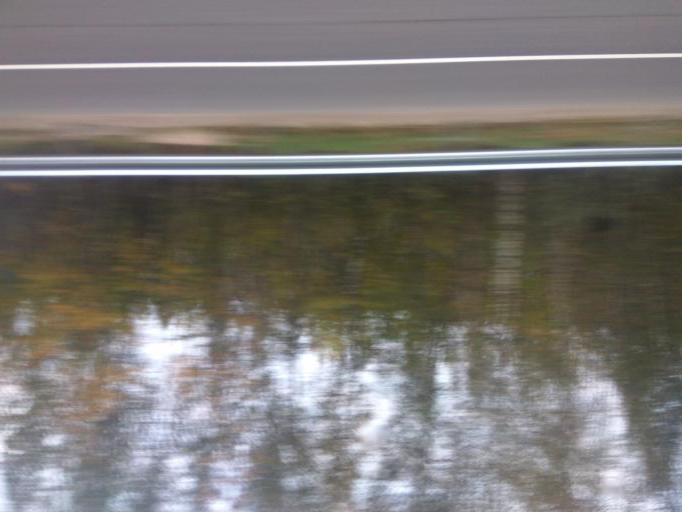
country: RU
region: Moskovskaya
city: Krasnoarmeysk
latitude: 56.0285
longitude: 38.1826
